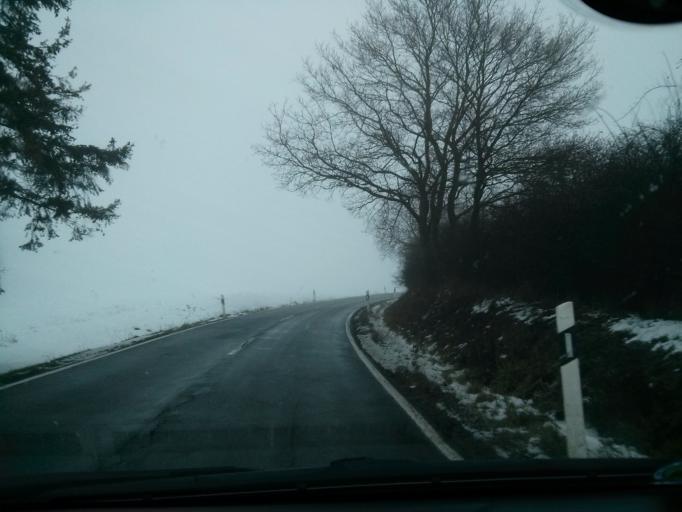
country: DE
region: Rheinland-Pfalz
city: Berg
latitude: 50.5675
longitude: 6.9548
